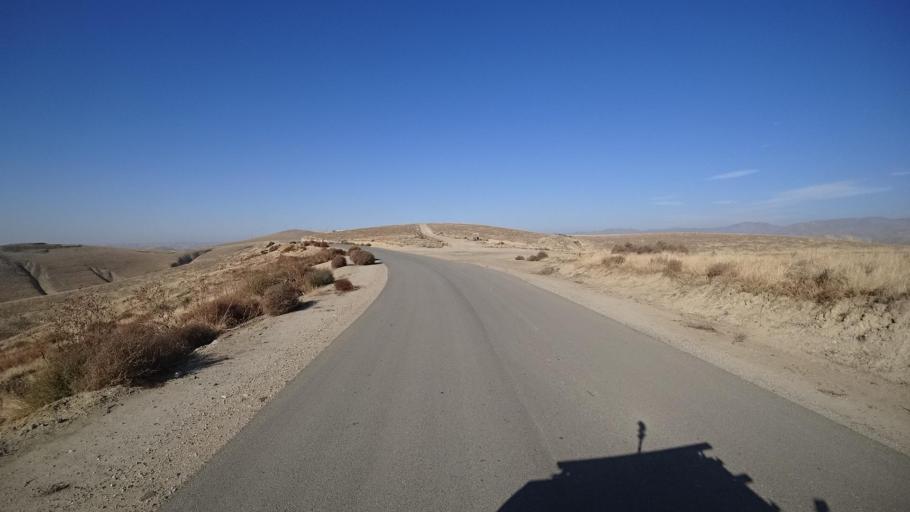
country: US
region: California
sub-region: Kern County
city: Oildale
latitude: 35.4825
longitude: -118.8757
